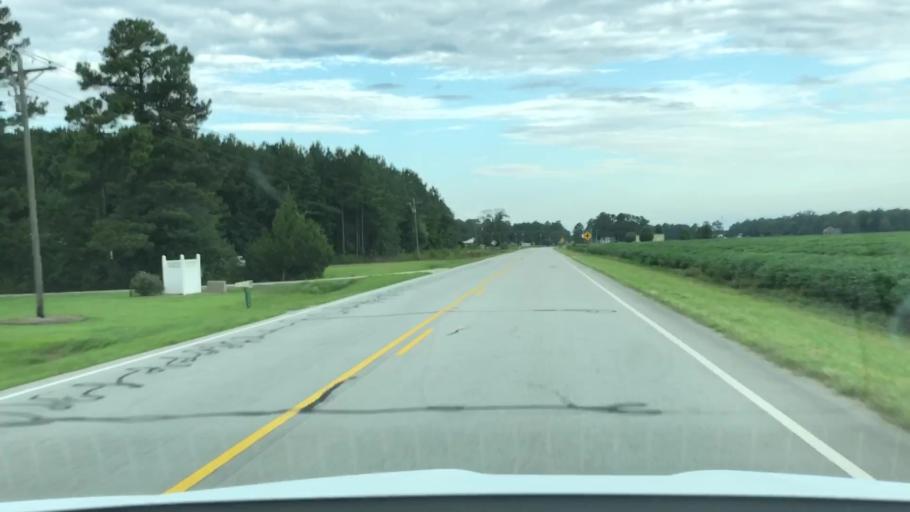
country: US
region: North Carolina
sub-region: Jones County
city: Trenton
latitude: 35.0852
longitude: -77.4464
